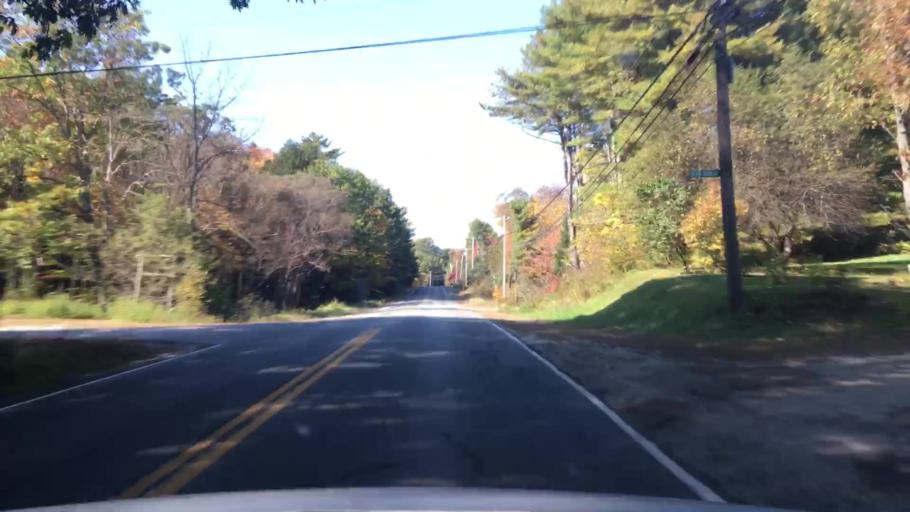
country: US
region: Maine
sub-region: Sagadahoc County
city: Topsham
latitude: 44.0340
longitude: -69.9542
